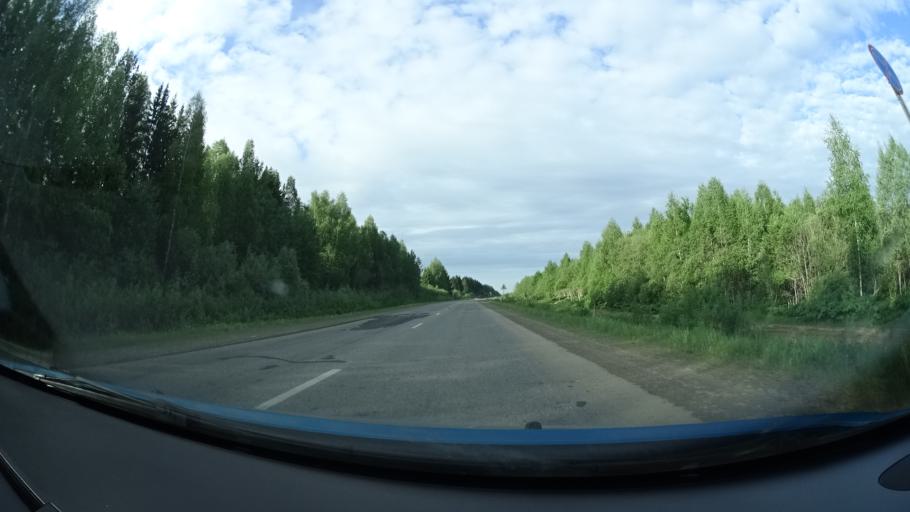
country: RU
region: Perm
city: Osa
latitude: 57.3560
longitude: 55.5992
